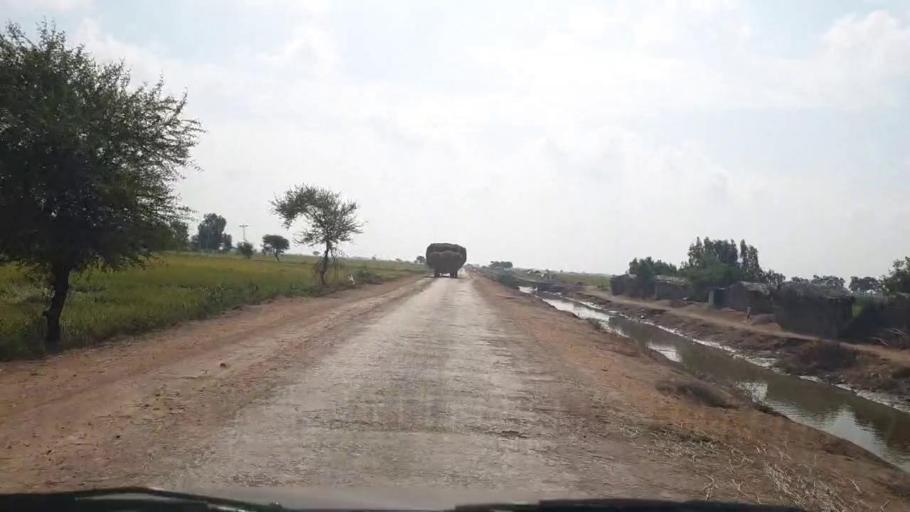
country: PK
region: Sindh
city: Kario
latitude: 24.5893
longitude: 68.5738
